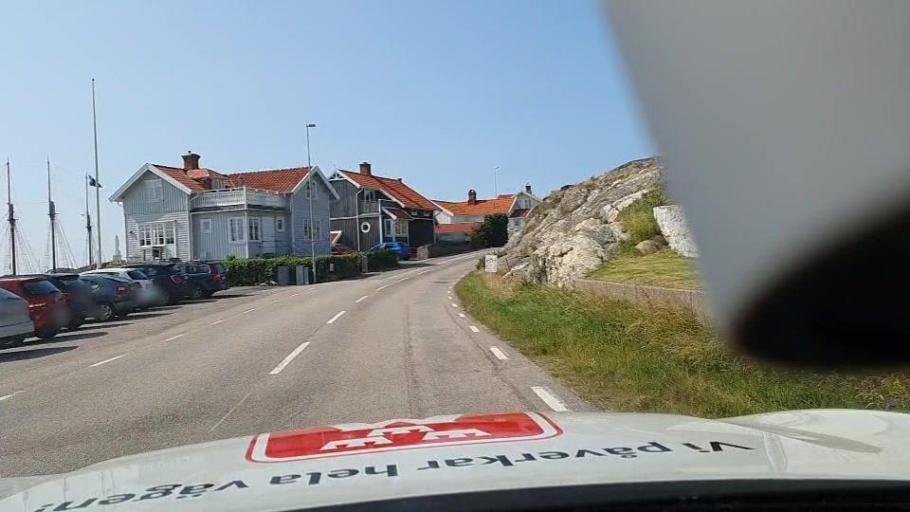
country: SE
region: Vaestra Goetaland
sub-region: Tjorns Kommun
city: Skaerhamn
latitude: 58.1077
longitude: 11.4679
